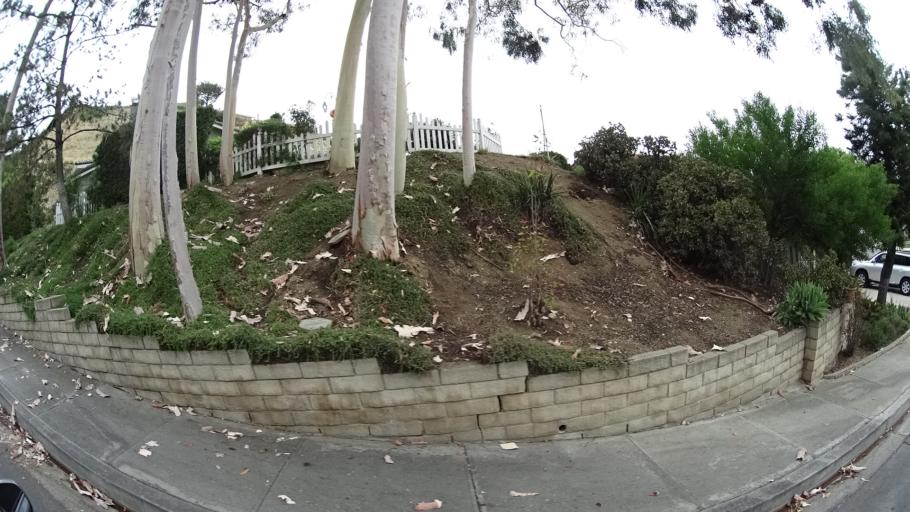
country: US
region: California
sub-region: Los Angeles County
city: Burbank
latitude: 34.2130
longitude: -118.3289
